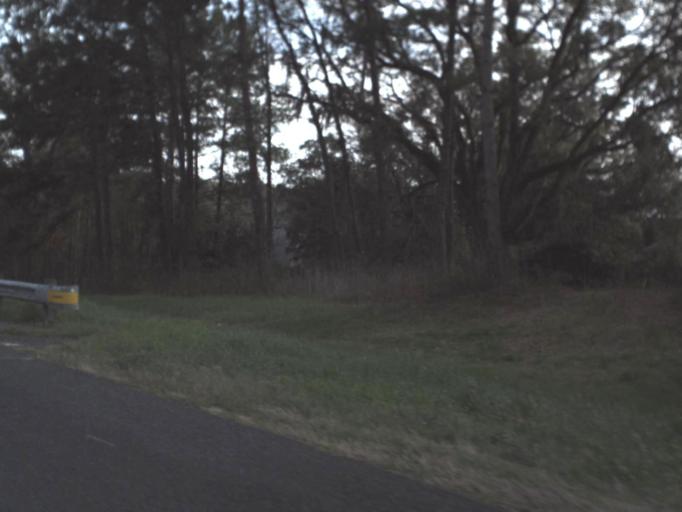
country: US
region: Florida
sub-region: Leon County
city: Tallahassee
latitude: 30.4801
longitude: -84.1501
